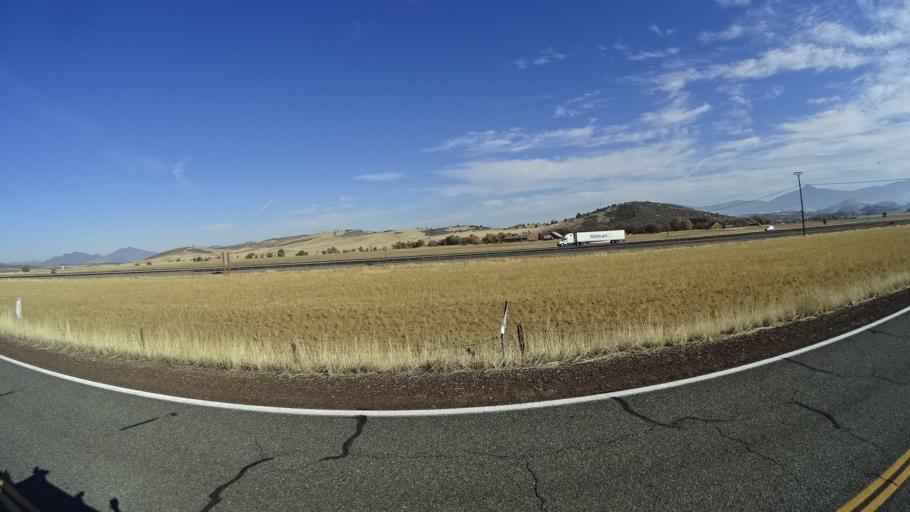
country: US
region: California
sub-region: Siskiyou County
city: Montague
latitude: 41.6473
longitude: -122.5412
